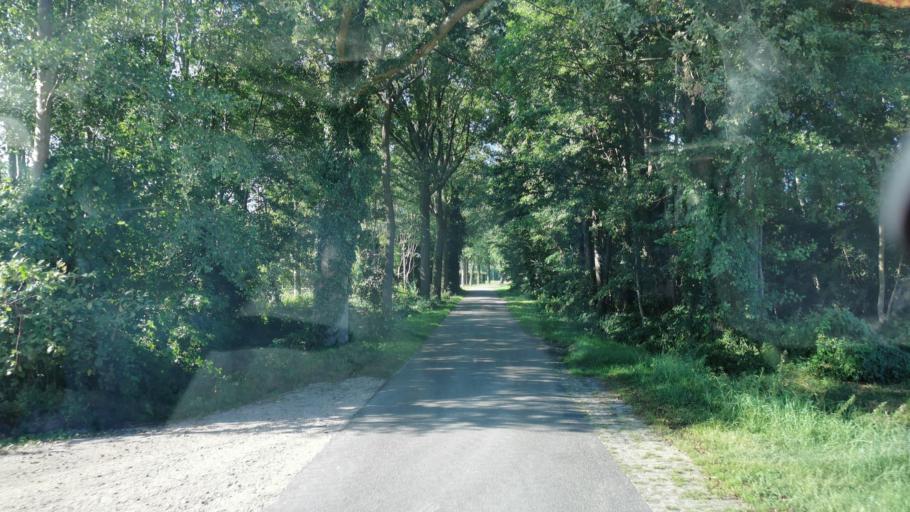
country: DE
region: Lower Saxony
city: Lage
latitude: 52.4181
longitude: 6.9478
